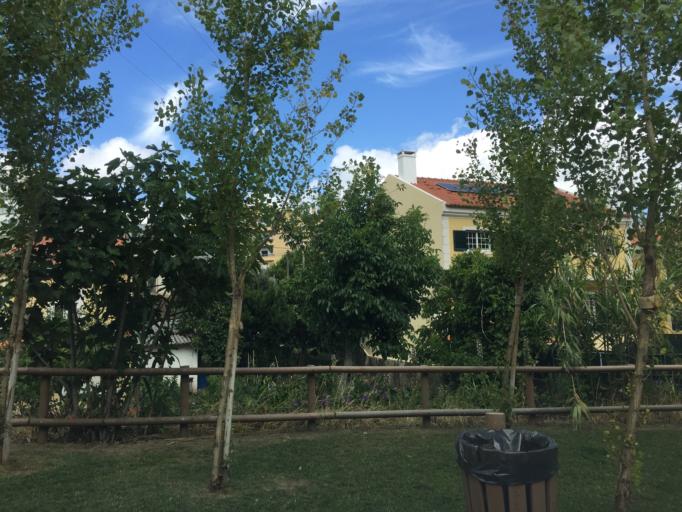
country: PT
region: Lisbon
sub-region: Odivelas
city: Famoes
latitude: 38.7883
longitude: -9.2279
